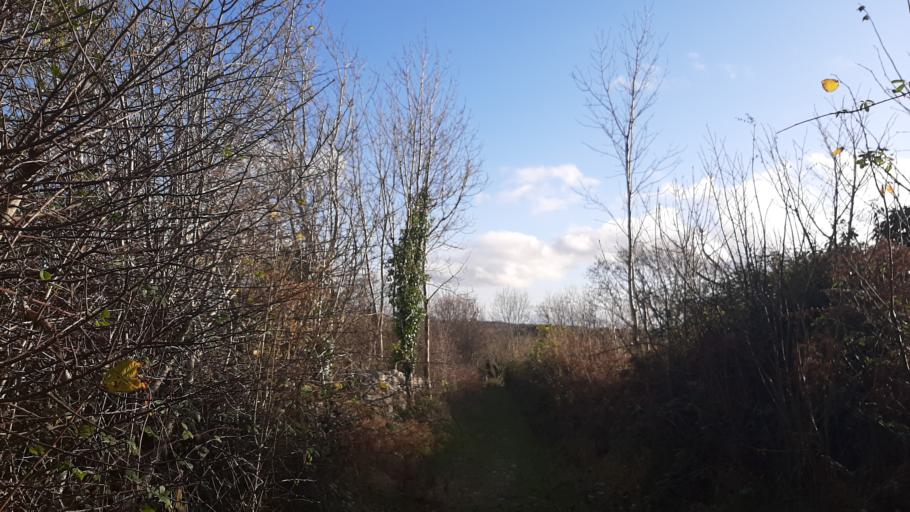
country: IE
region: Connaught
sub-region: County Galway
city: Gaillimh
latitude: 53.3017
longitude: -9.0597
